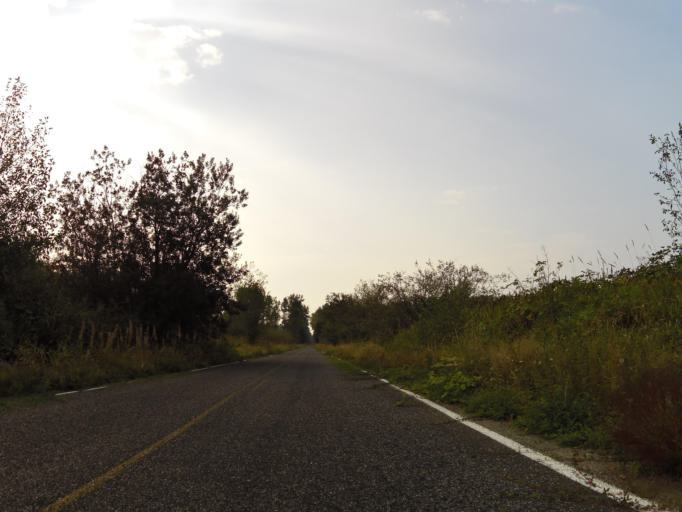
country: US
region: Washington
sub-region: Whatcom County
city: Birch Bay
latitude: 48.8771
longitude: -122.7317
